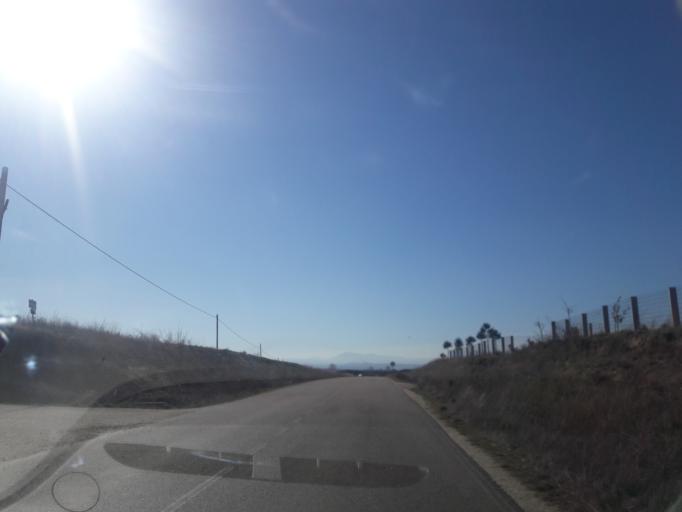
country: ES
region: Castille and Leon
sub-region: Provincia de Salamanca
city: Macotera
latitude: 40.8405
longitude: -5.3067
